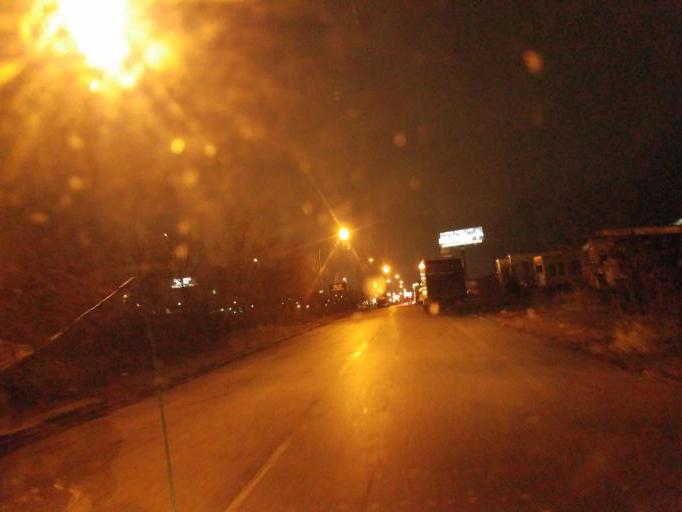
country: US
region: Illinois
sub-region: Madison County
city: Venice
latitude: 38.6591
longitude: -90.1952
